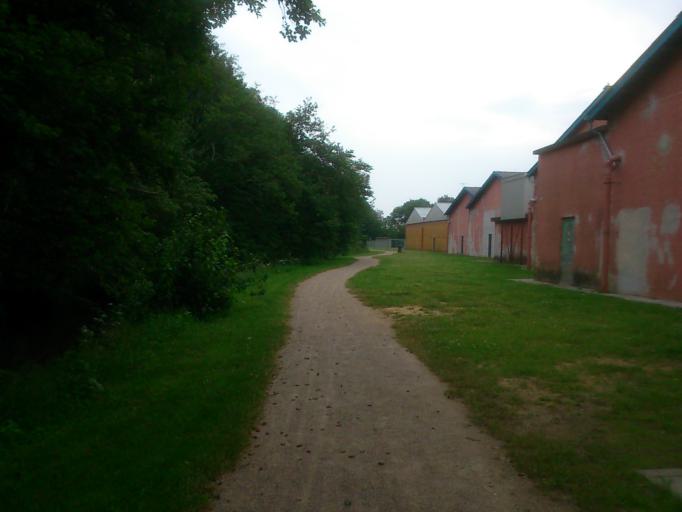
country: DK
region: Central Jutland
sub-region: Ringkobing-Skjern Kommune
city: Tarm
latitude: 55.9044
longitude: 8.5229
